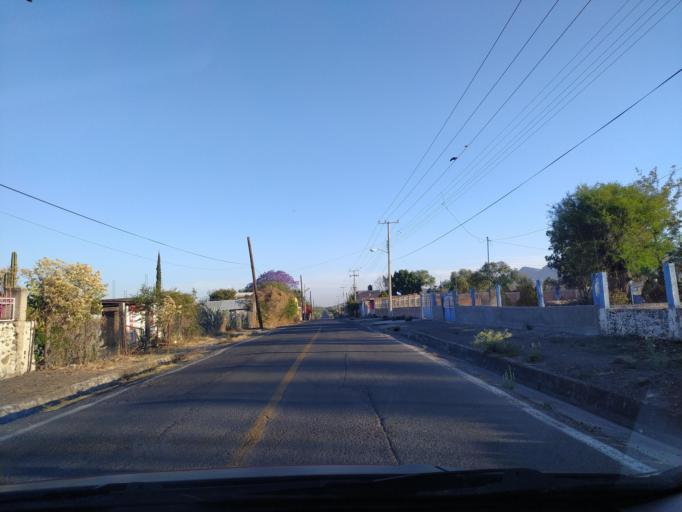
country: MX
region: Guanajuato
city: Ciudad Manuel Doblado
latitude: 20.7497
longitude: -101.8247
